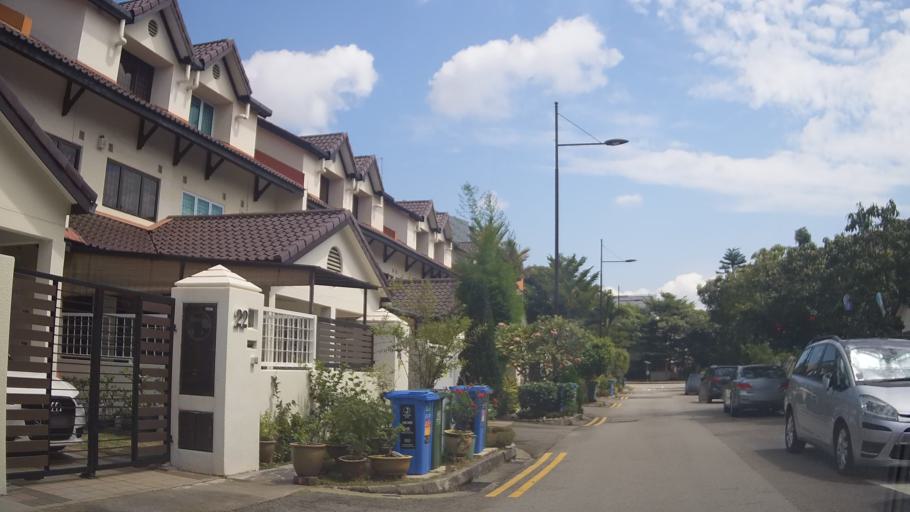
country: SG
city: Singapore
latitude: 1.3242
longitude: 103.9518
